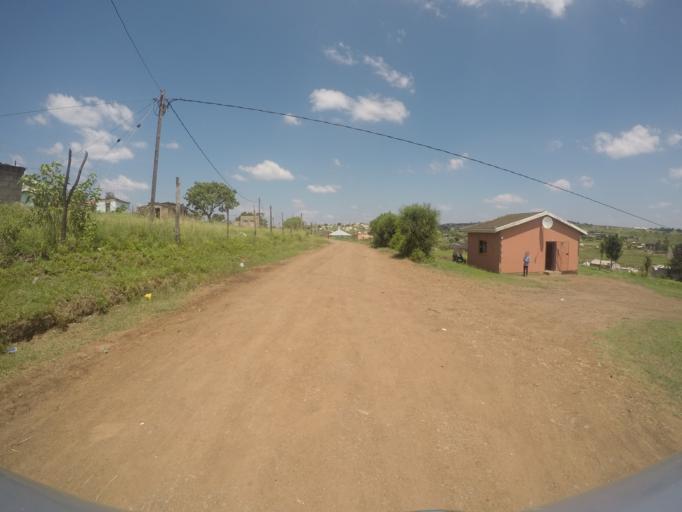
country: ZA
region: KwaZulu-Natal
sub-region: uThungulu District Municipality
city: Empangeni
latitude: -28.6027
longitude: 31.7410
